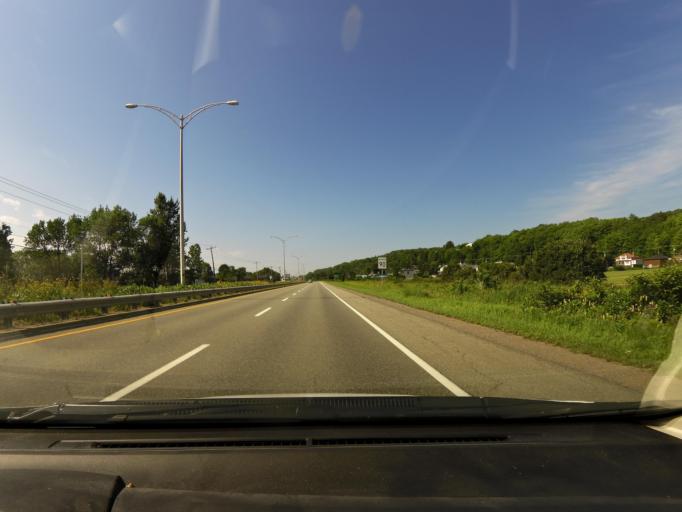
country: CA
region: Quebec
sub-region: Capitale-Nationale
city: Chateau-Richer
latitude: 46.9828
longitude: -71.0017
